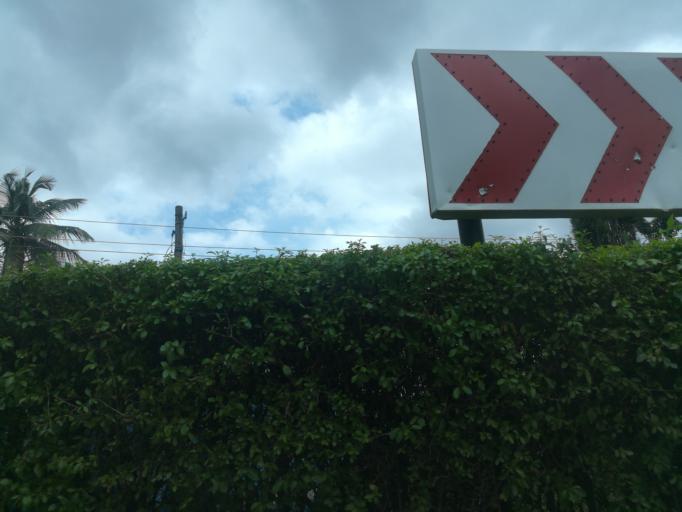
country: NG
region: Lagos
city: Somolu
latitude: 6.5519
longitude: 3.3620
